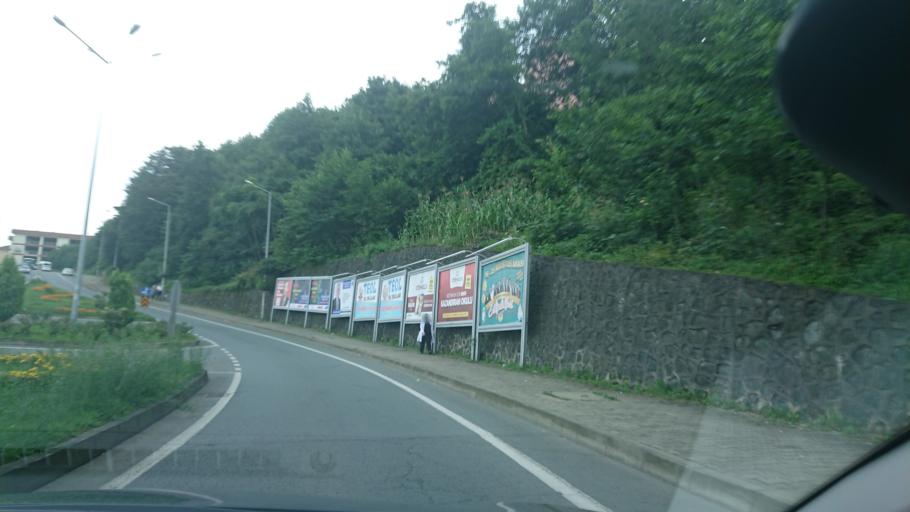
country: TR
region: Rize
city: Gundogdu
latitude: 41.0378
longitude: 40.5692
